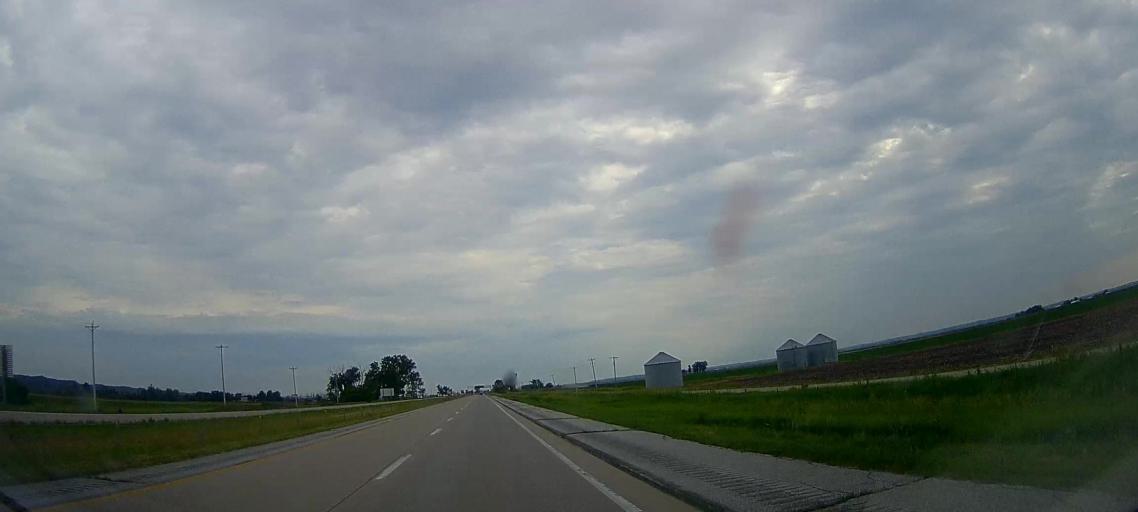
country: US
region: Iowa
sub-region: Harrison County
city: Missouri Valley
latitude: 41.5300
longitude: -95.9179
